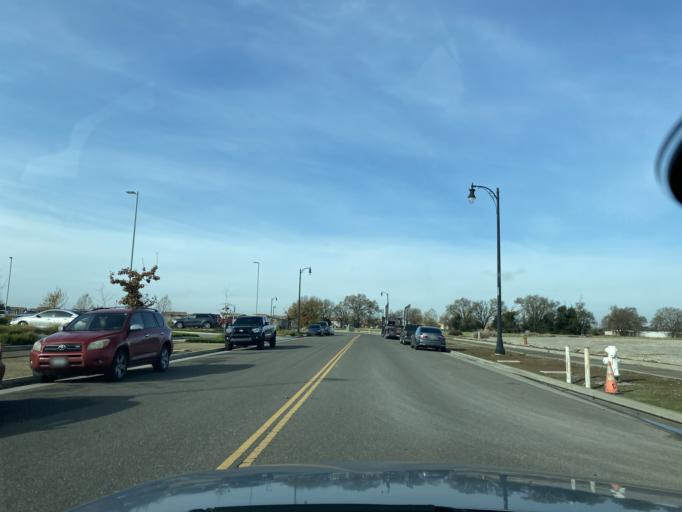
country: US
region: California
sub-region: Sacramento County
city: Elk Grove
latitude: 38.4036
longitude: -121.3927
